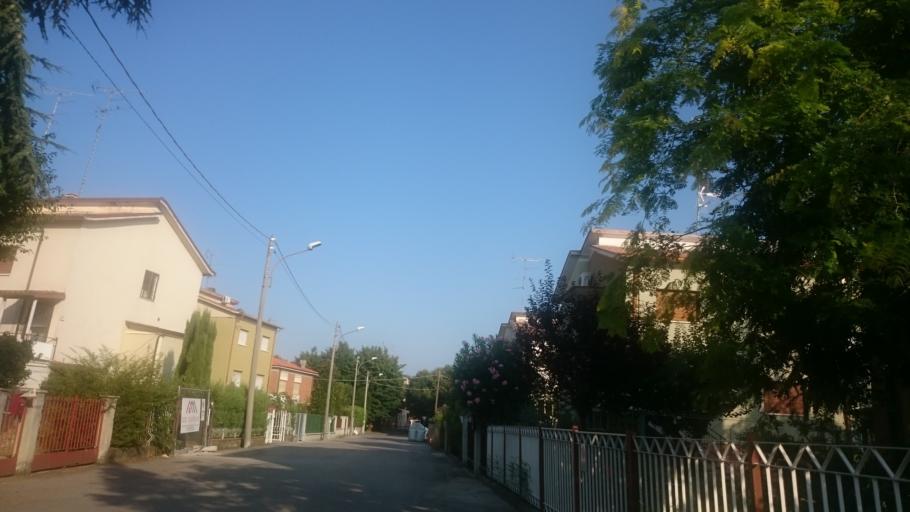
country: IT
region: Emilia-Romagna
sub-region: Provincia di Reggio Emilia
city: Scandiano
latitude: 44.5967
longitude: 10.6927
